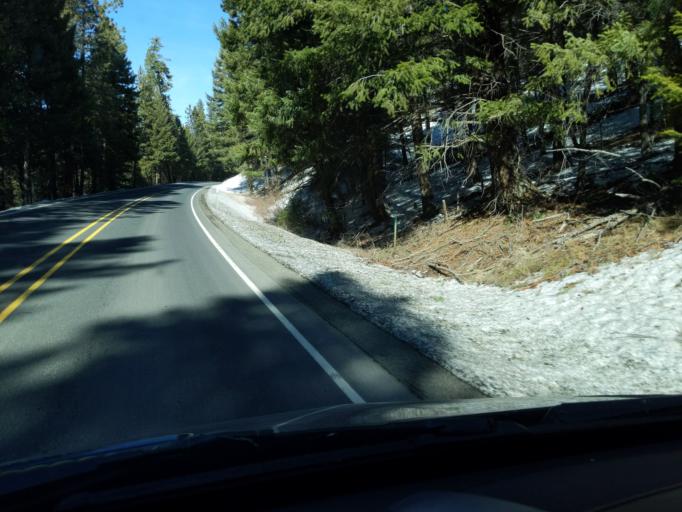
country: US
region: Oregon
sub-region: Grant County
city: John Day
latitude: 44.8849
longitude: -119.0140
